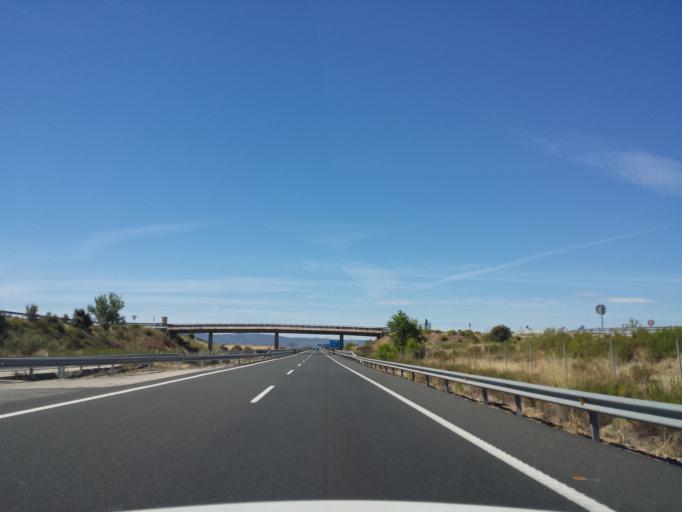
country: ES
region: Extremadura
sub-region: Provincia de Caceres
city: Saucedilla
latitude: 39.8396
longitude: -5.6459
